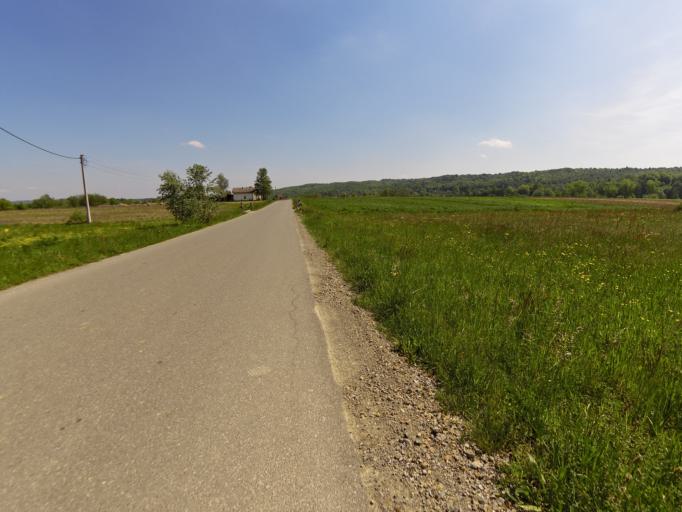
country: HR
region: Karlovacka
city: Ozalj
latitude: 45.5634
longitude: 15.4853
